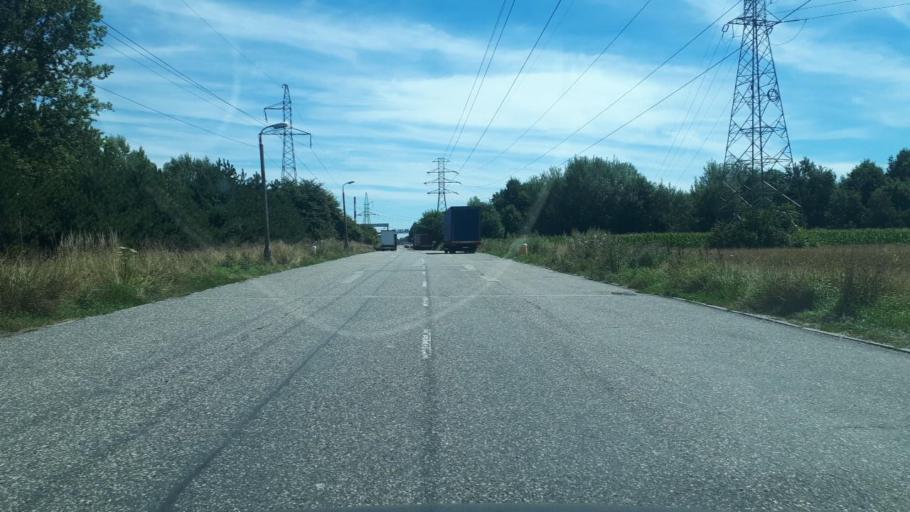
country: PL
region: Silesian Voivodeship
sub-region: Powiat bierunsko-ledzinski
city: Bierun
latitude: 50.1062
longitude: 19.0568
